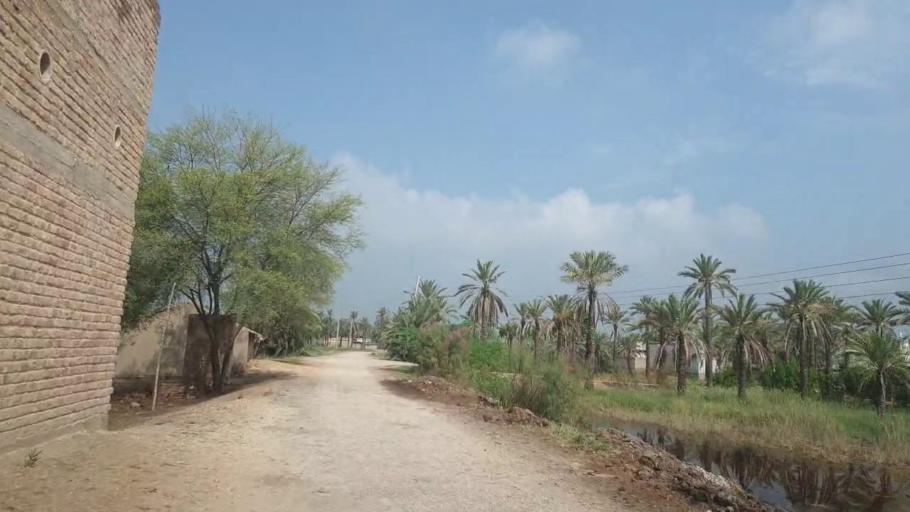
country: PK
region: Sindh
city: Khairpur
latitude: 27.5571
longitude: 68.7587
